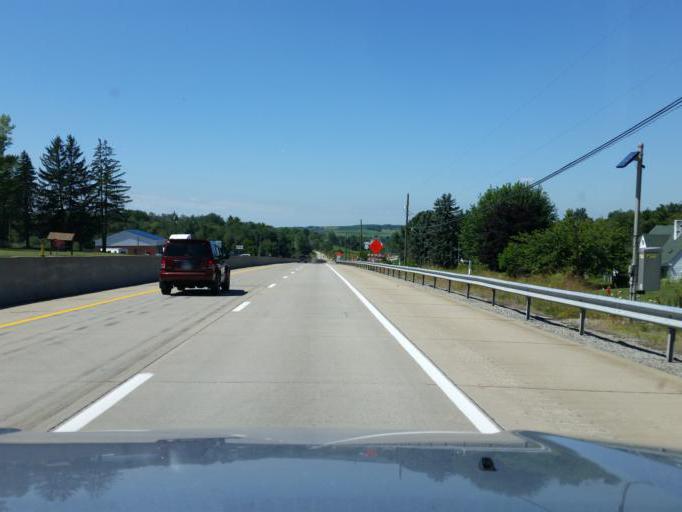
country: US
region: Pennsylvania
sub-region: Westmoreland County
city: Latrobe
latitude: 40.4051
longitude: -79.4057
